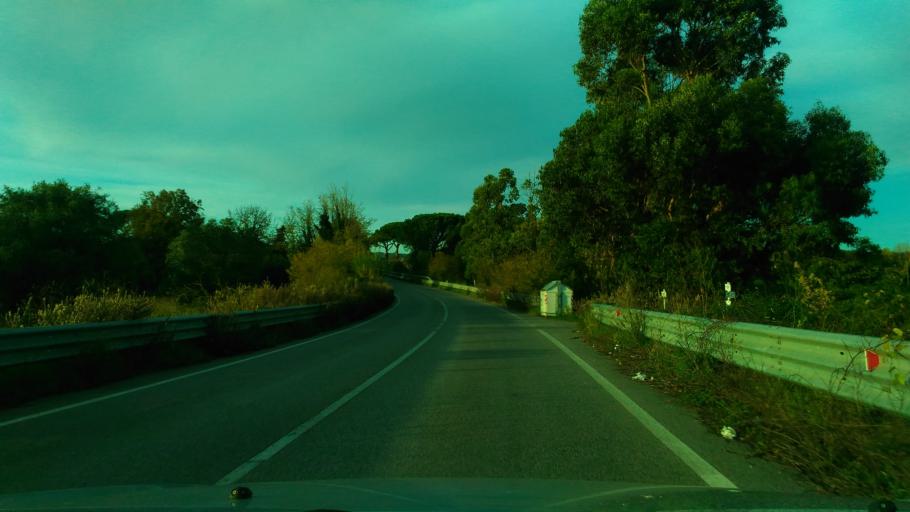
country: IT
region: Tuscany
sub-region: Provincia di Livorno
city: S.P. in Palazzi
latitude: 43.3618
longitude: 10.5101
